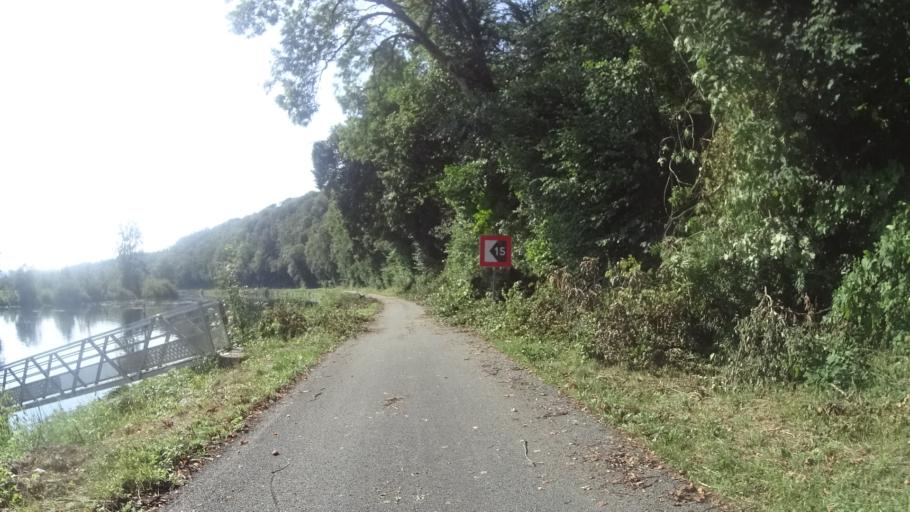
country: FR
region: Franche-Comte
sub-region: Departement du Doubs
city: Clerval
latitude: 47.4347
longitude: 6.5318
